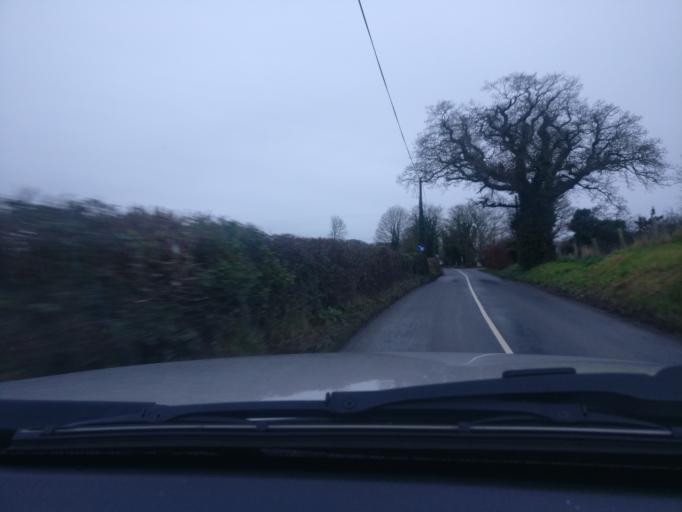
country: IE
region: Leinster
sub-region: An Mhi
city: Dunshaughlin
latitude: 53.4827
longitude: -6.6140
